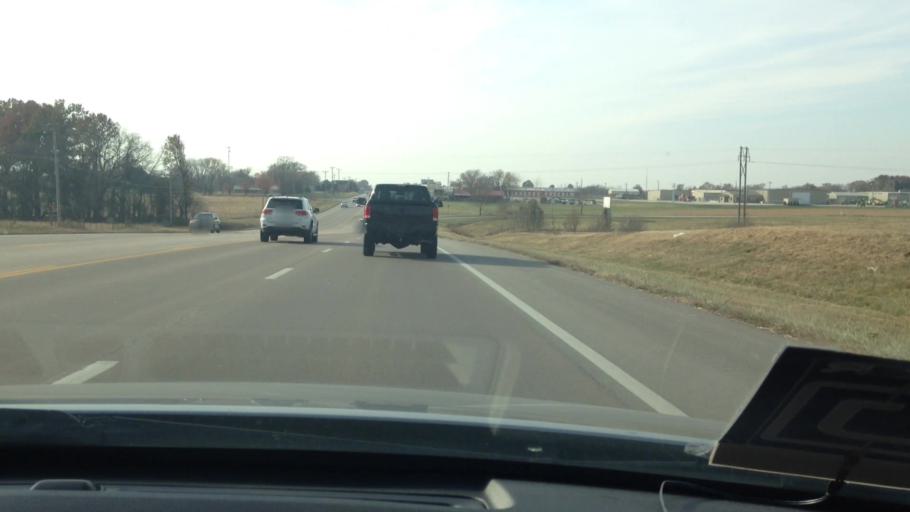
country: US
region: Missouri
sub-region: Henry County
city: Clinton
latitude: 38.3891
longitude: -93.7878
